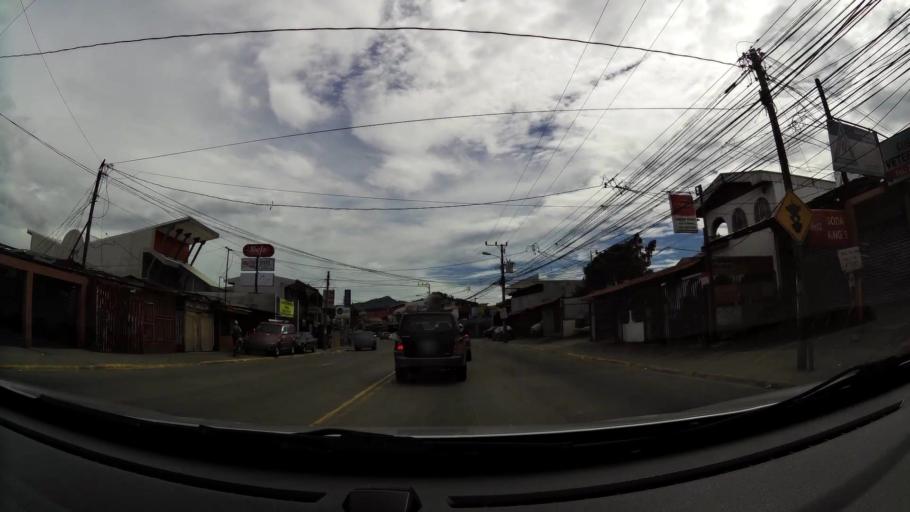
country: CR
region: San Jose
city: San Pedro
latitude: 9.9090
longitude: -84.0533
